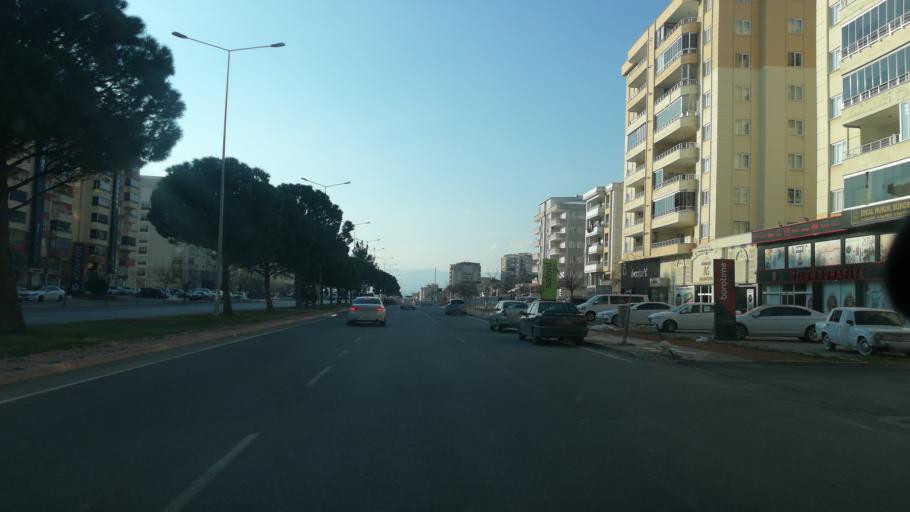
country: TR
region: Kahramanmaras
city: Kahramanmaras
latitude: 37.5951
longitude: 36.8533
